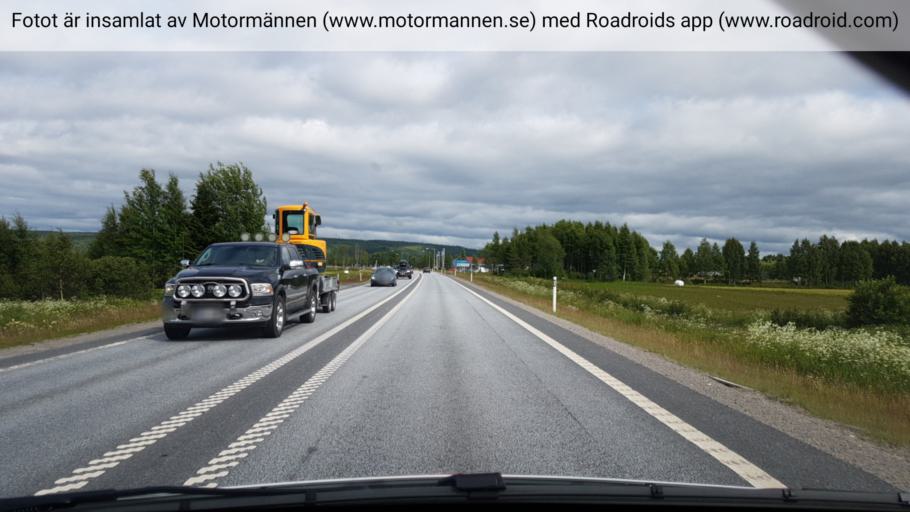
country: SE
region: Vaesterbotten
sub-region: Vannas Kommun
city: Vannasby
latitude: 63.9203
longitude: 19.8222
